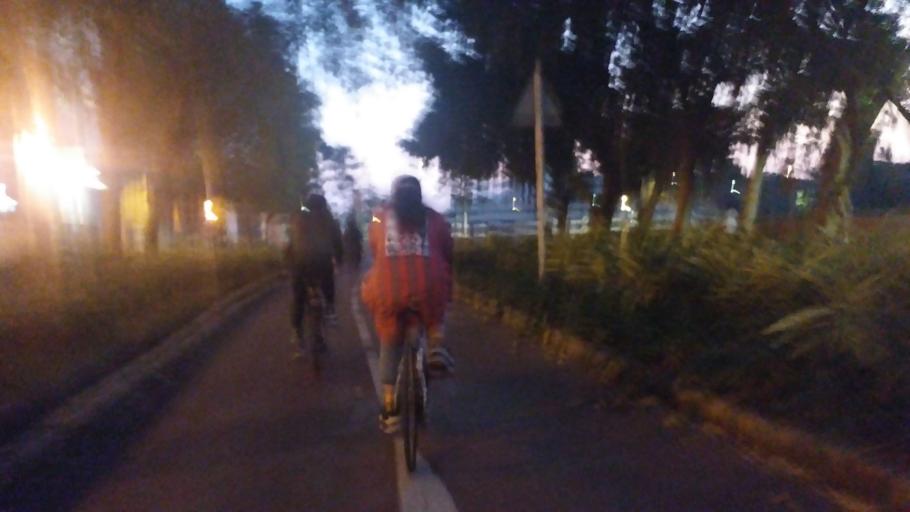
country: HK
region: Yuen Long
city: Yuen Long Kau Hui
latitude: 22.4633
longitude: 113.9952
